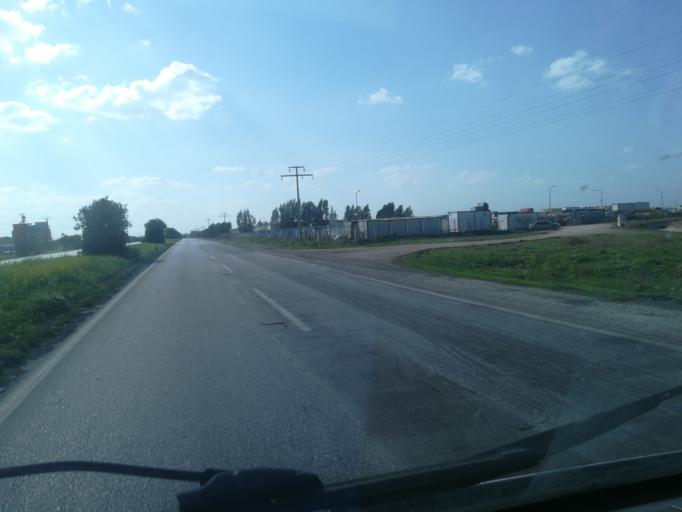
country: TR
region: Adana
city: Ceyhan
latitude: 37.0539
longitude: 35.8532
